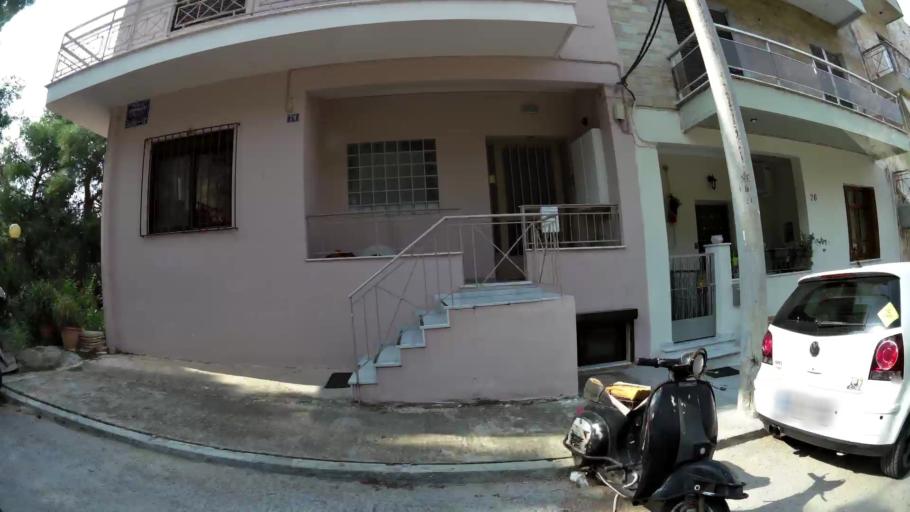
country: GR
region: Attica
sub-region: Nomarchia Athinas
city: Galatsi
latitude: 38.0063
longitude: 23.7536
